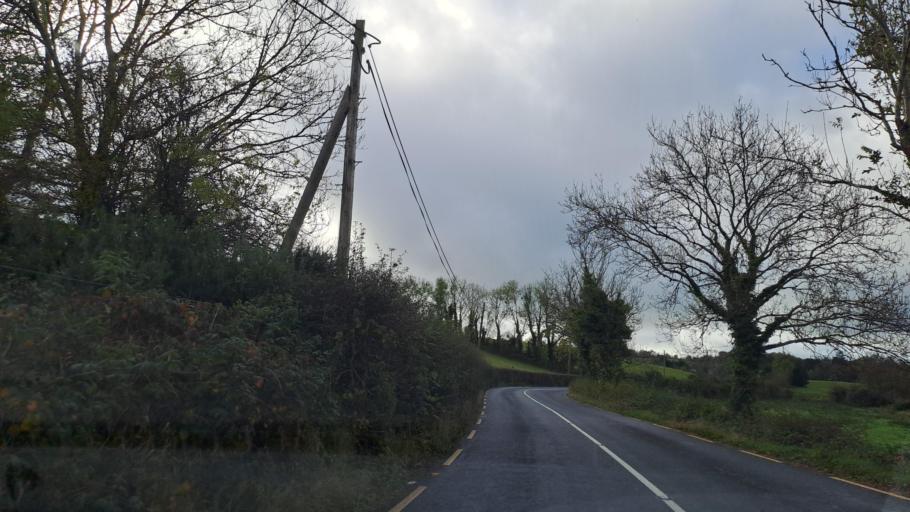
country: IE
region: Ulster
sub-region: An Cabhan
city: Virginia
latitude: 53.8682
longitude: -7.0407
